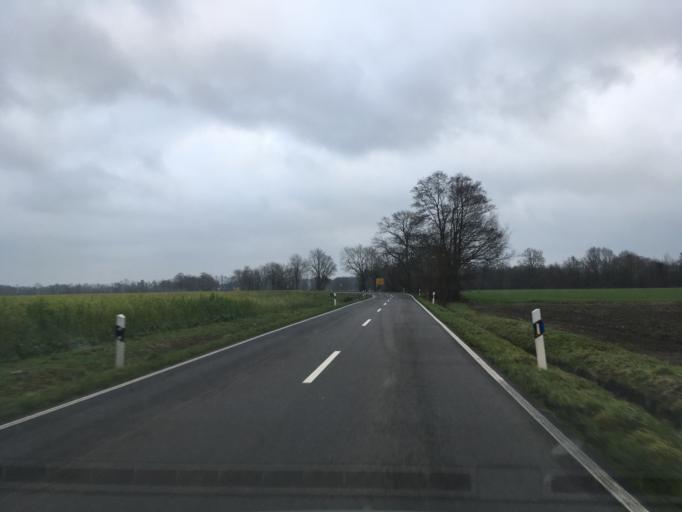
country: DE
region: North Rhine-Westphalia
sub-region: Regierungsbezirk Munster
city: Heek
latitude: 52.1621
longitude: 7.1252
